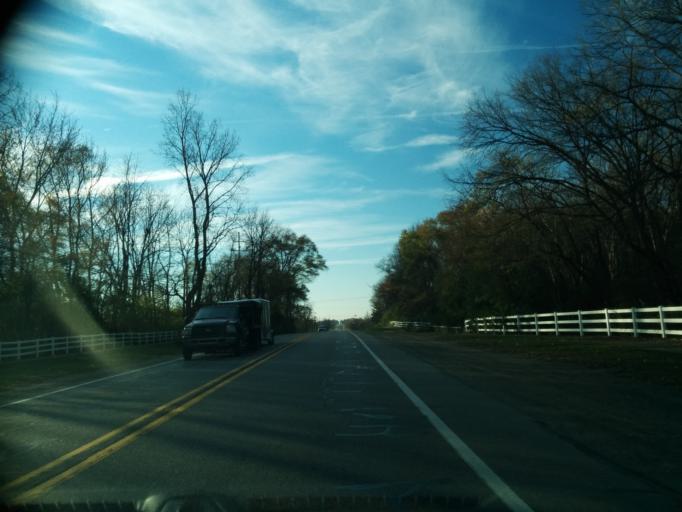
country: US
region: Michigan
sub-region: Oakland County
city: Farmington Hills
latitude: 42.4803
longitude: -83.4164
